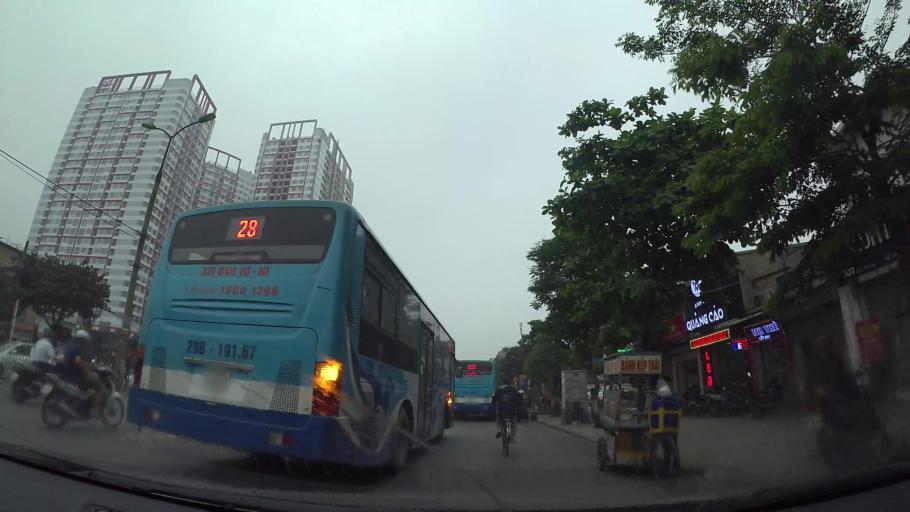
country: VN
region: Ha Noi
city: Hai BaTrung
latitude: 20.9845
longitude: 105.8412
